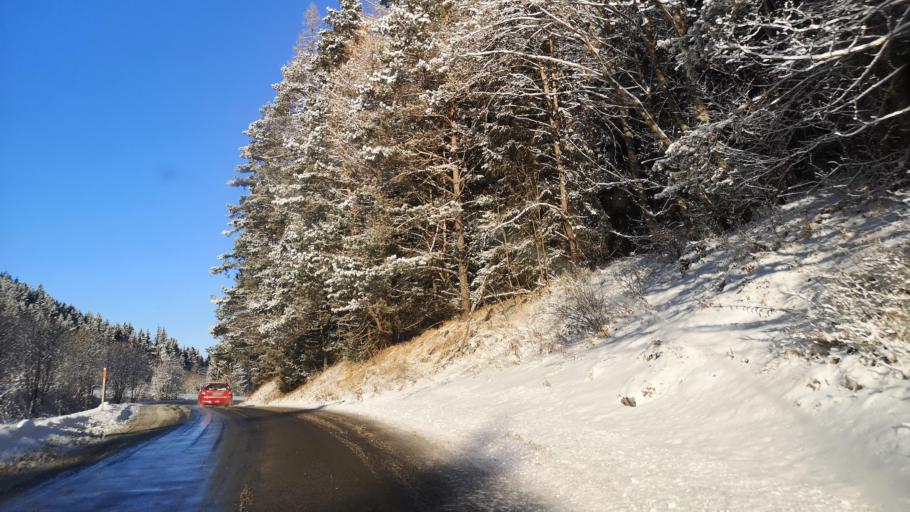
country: SK
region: Banskobystricky
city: Revuca
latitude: 48.8273
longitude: 20.1252
